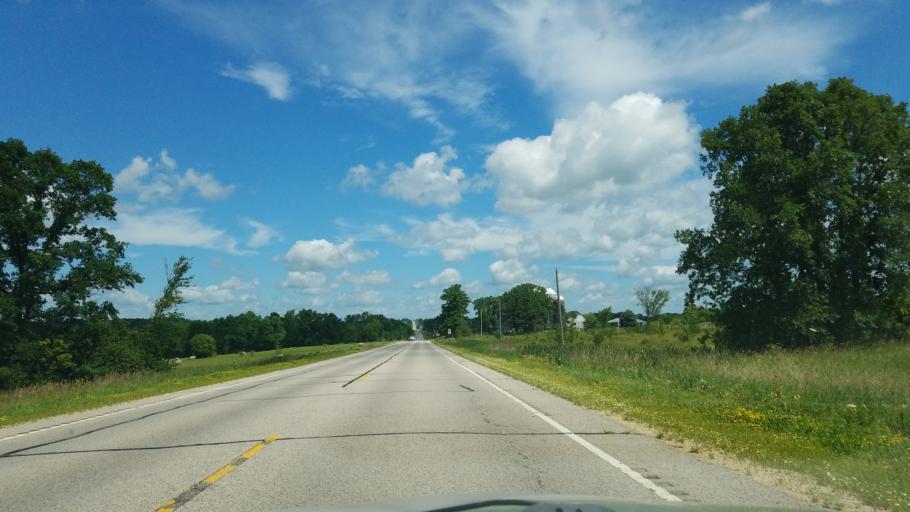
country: US
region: Wisconsin
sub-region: Saint Croix County
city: Glenwood City
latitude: 44.9841
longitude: -92.1965
